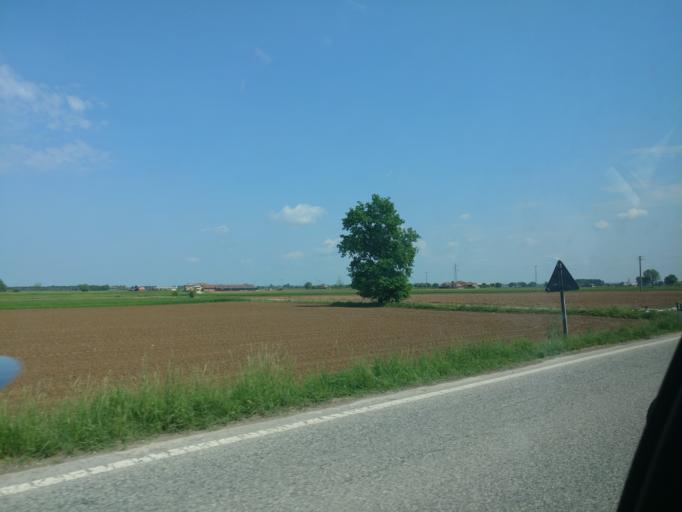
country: IT
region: Piedmont
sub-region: Provincia di Torino
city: Cavour
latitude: 44.7583
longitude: 7.4008
